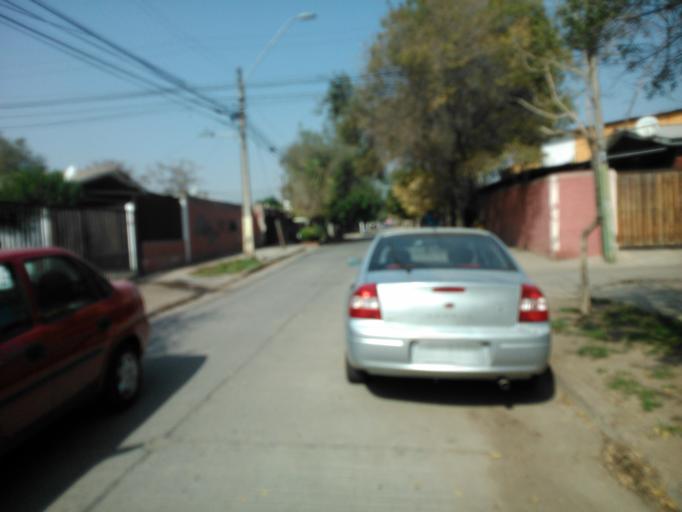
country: CL
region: Santiago Metropolitan
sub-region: Provincia de Cordillera
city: Puente Alto
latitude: -33.5573
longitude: -70.5833
